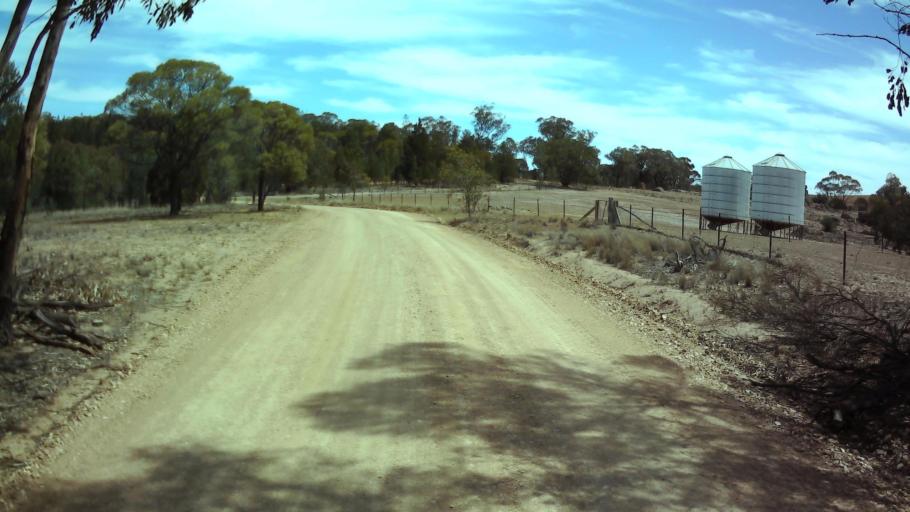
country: AU
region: New South Wales
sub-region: Weddin
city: Grenfell
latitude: -33.8099
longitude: 148.1577
